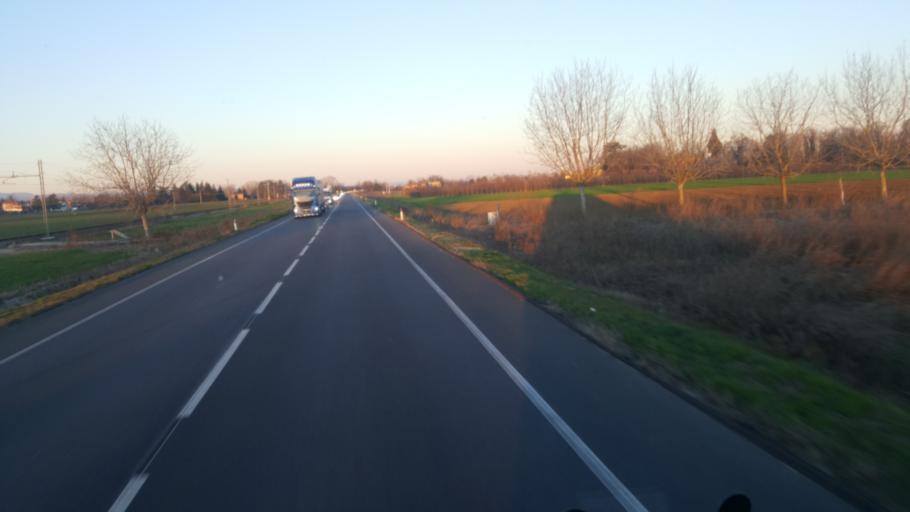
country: IT
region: Emilia-Romagna
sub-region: Provincia di Bologna
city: Bazzano
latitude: 44.5118
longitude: 11.0971
